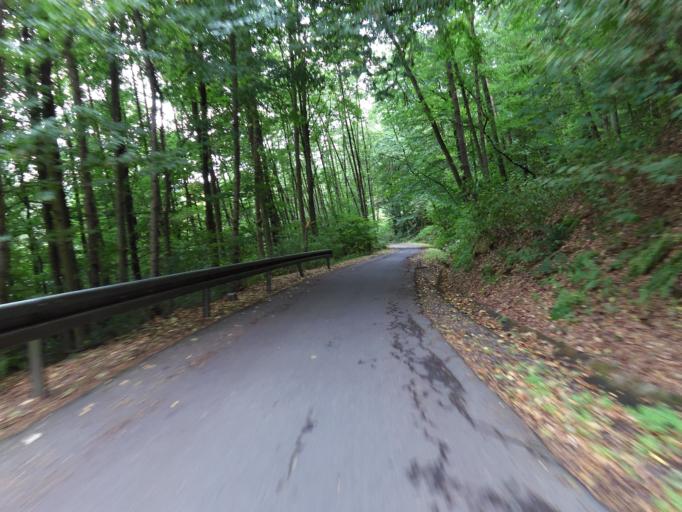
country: DE
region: Hesse
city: Hochst im Odenwald
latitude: 49.8132
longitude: 9.0178
